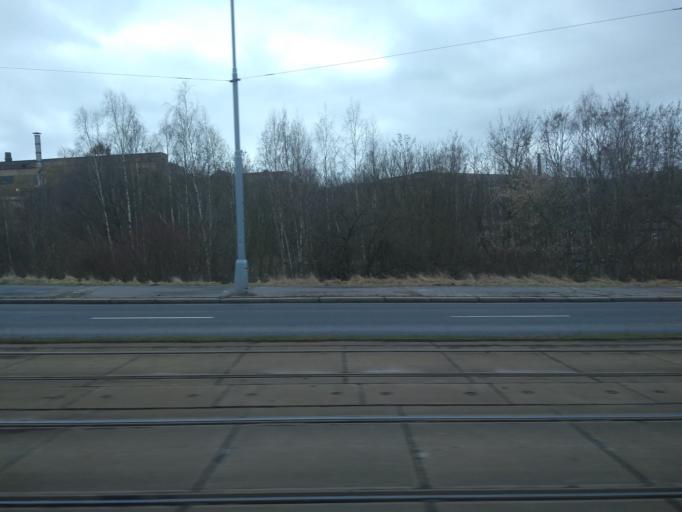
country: CZ
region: Plzensky
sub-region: Okres Plzen-Mesto
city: Pilsen
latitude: 49.7467
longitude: 13.3552
